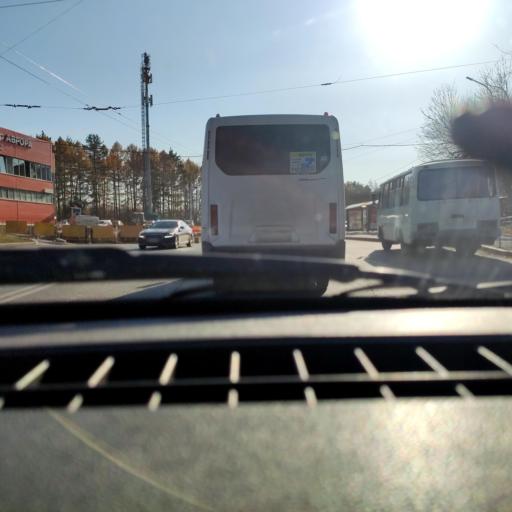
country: RU
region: Bashkortostan
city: Ufa
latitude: 54.6971
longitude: 56.0067
